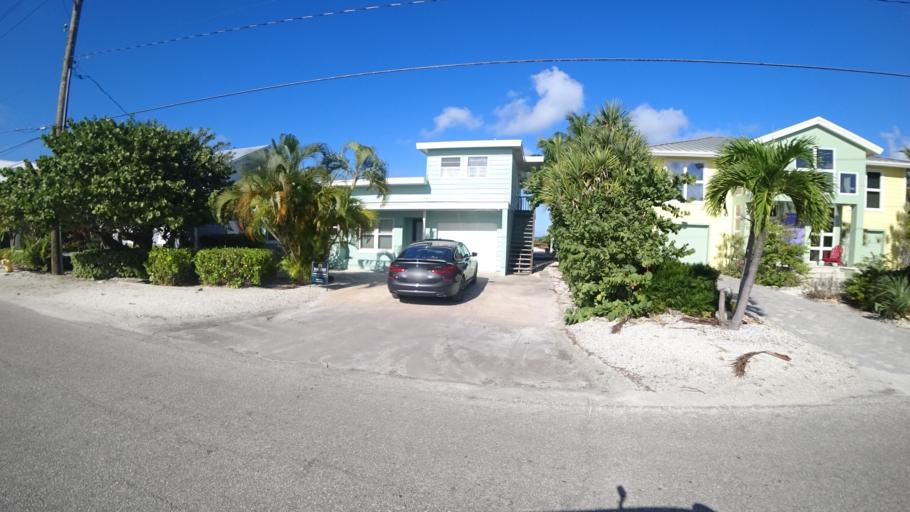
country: US
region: Florida
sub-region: Manatee County
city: Anna Maria
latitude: 27.5308
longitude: -82.7281
